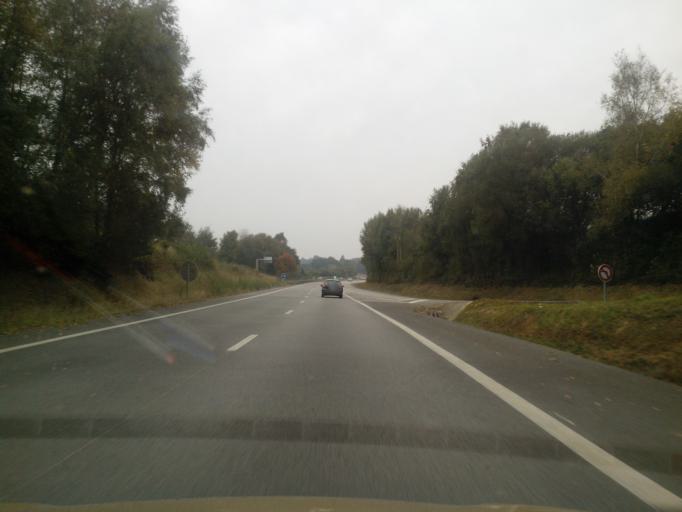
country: FR
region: Brittany
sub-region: Departement du Morbihan
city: Locmine
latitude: 47.8982
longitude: -2.8405
